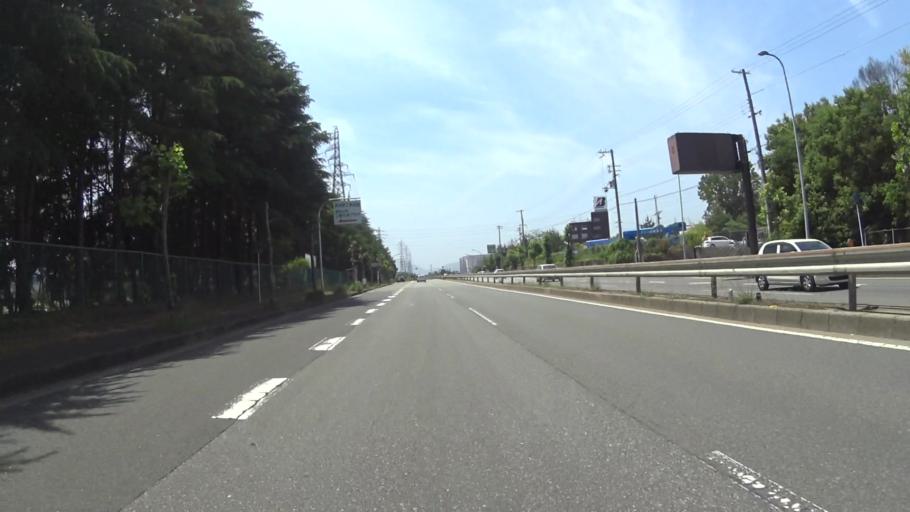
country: JP
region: Kyoto
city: Fukuchiyama
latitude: 35.2835
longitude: 135.1759
